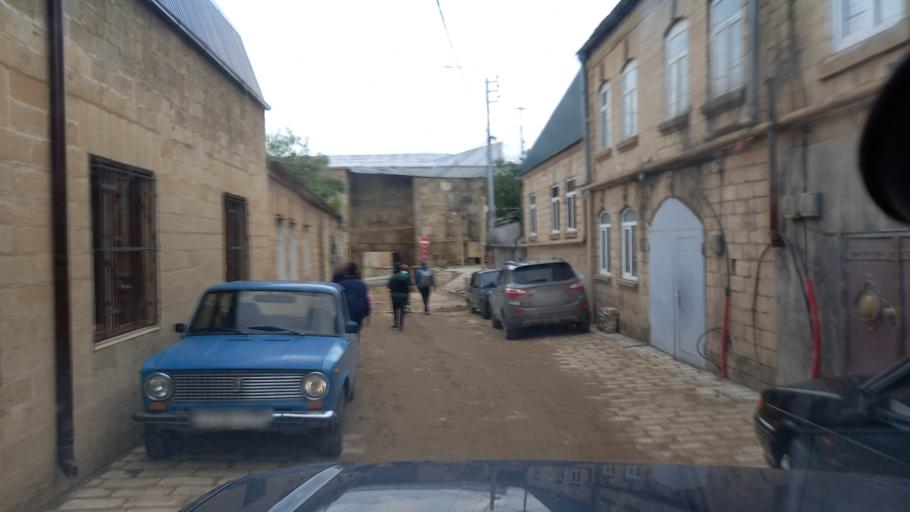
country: RU
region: Dagestan
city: Derbent
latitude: 42.0546
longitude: 48.2805
